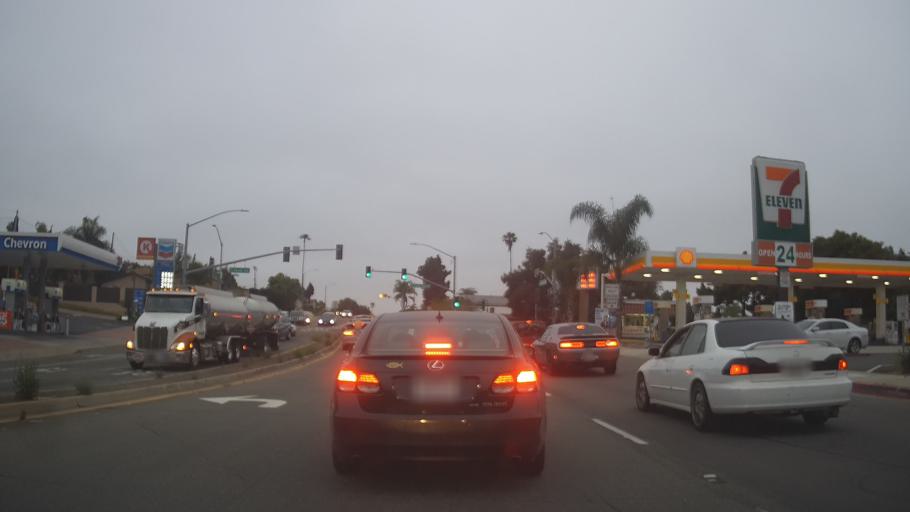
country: US
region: California
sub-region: San Diego County
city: Bonita
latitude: 32.6288
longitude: -117.0461
